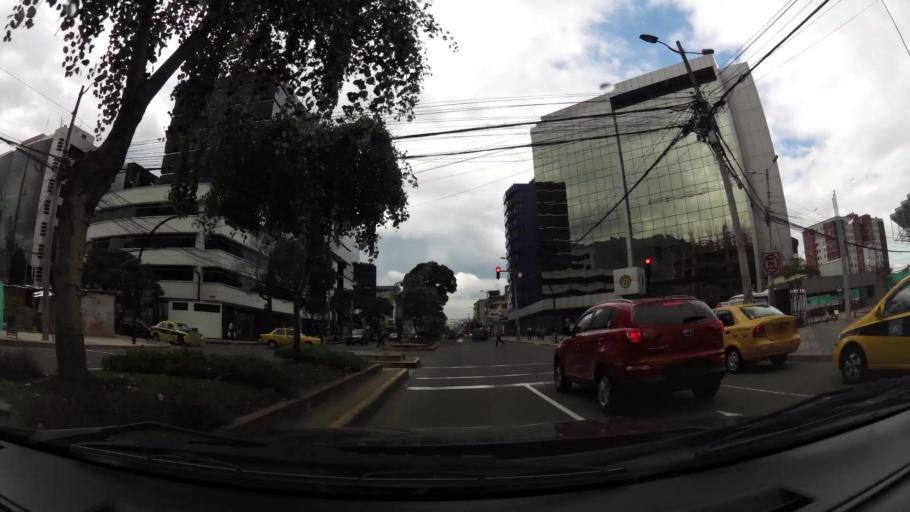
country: EC
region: Pichincha
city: Quito
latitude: -0.1719
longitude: -78.4848
